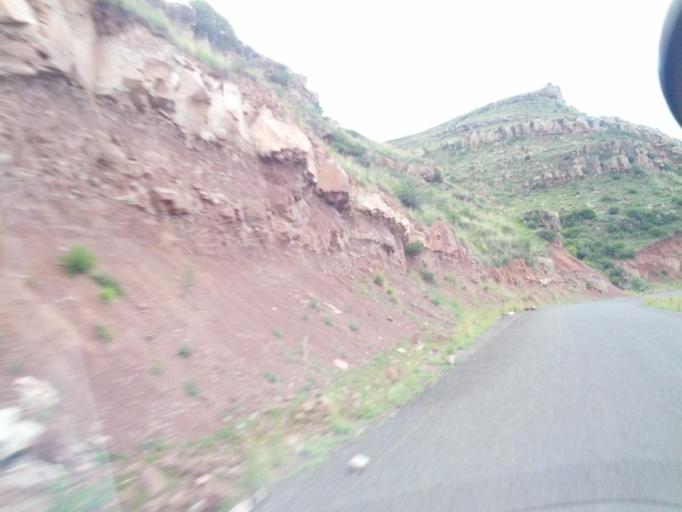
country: LS
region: Qacha's Nek
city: Qacha's Nek
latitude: -30.0596
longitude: 28.5040
